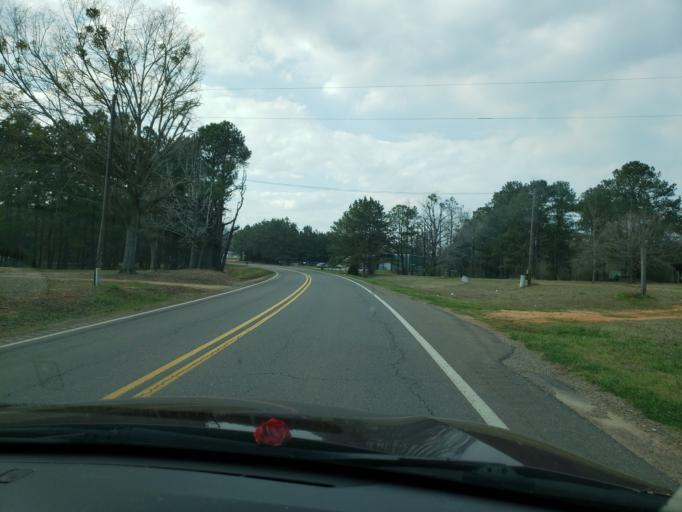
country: US
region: Alabama
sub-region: Hale County
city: Greensboro
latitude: 32.7205
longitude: -87.6219
